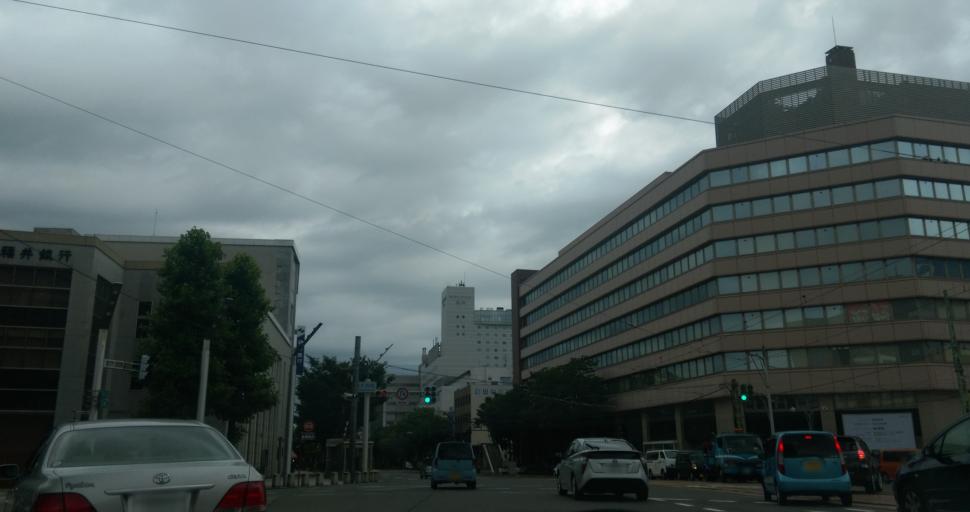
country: JP
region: Fukui
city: Fukui-shi
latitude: 36.0622
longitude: 136.2173
